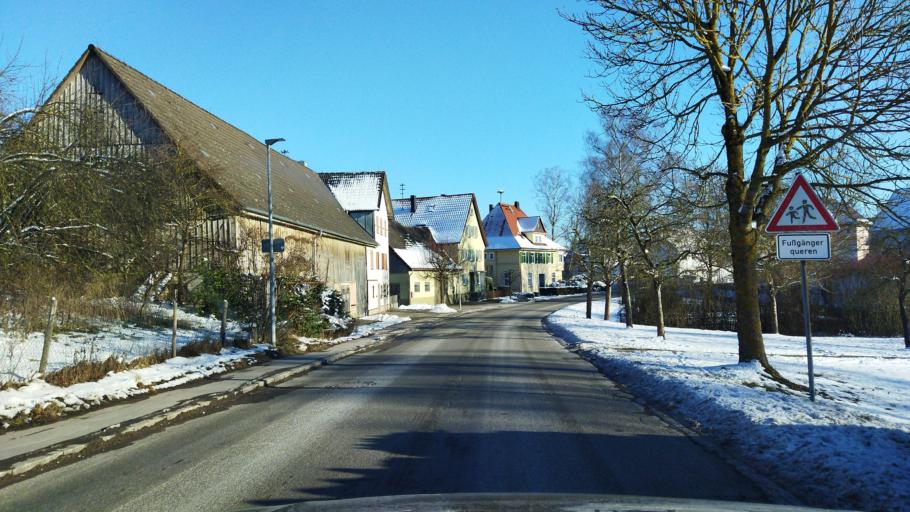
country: DE
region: Baden-Wuerttemberg
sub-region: Regierungsbezirk Stuttgart
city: Obersontheim
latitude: 49.0674
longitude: 9.8894
